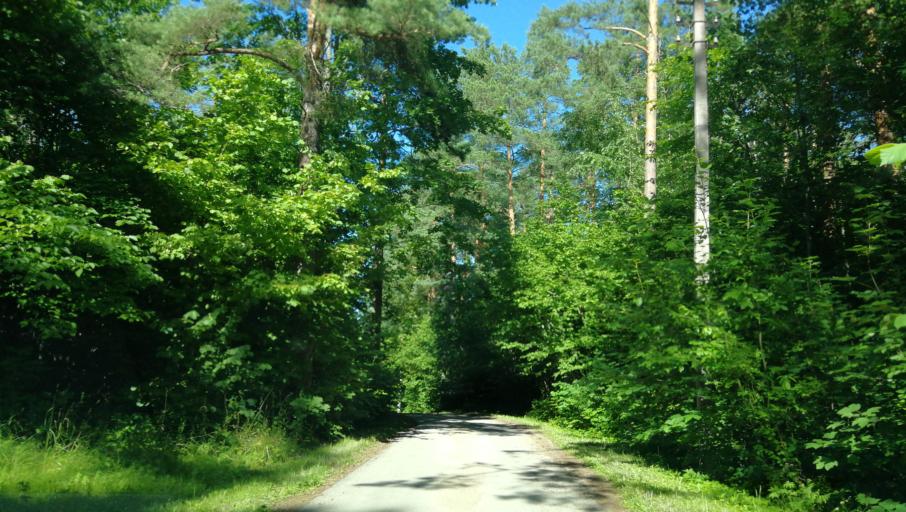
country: LV
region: Cesvaine
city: Cesvaine
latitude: 56.9705
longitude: 26.3178
